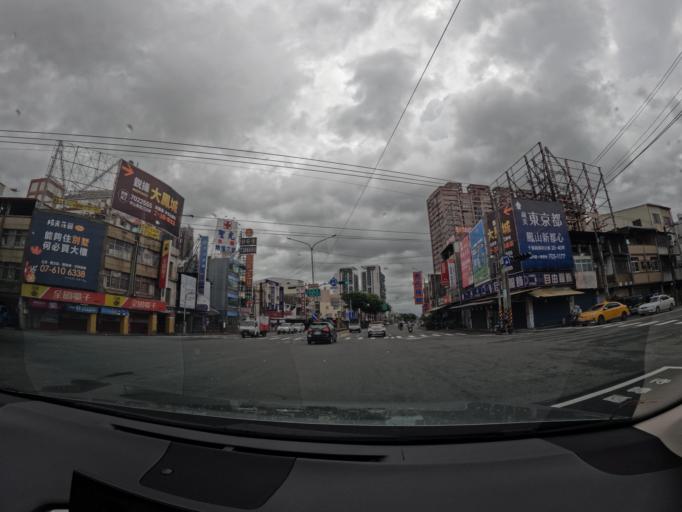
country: TW
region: Taiwan
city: Fengshan
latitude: 22.6228
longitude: 120.3680
